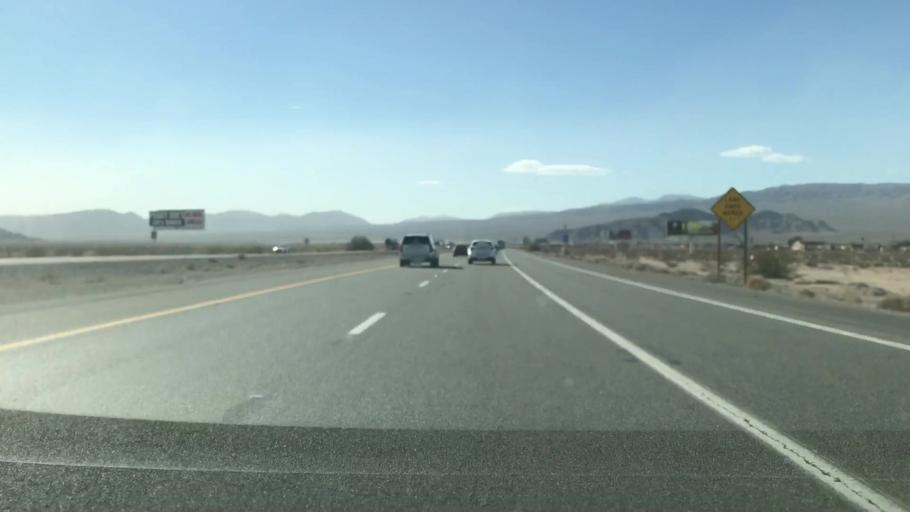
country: US
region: California
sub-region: San Bernardino County
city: Fort Irwin
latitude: 35.2769
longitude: -116.0523
